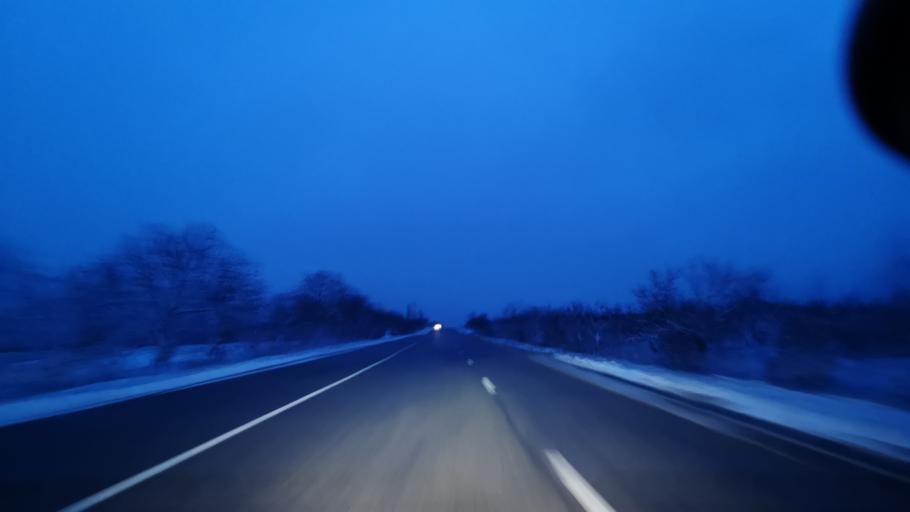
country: MD
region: Orhei
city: Orhei
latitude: 47.5409
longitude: 28.7932
